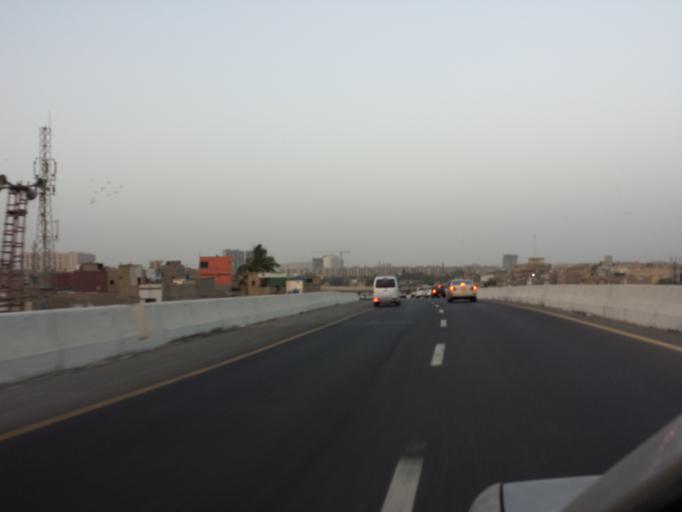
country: PK
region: Sindh
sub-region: Karachi District
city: Karachi
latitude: 24.8997
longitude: 67.0596
